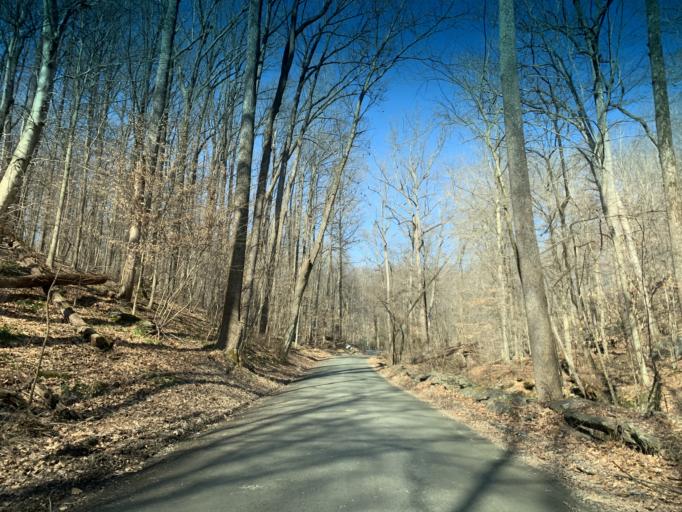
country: US
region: Maryland
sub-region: Harford County
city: Fallston
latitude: 39.5100
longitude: -76.4304
